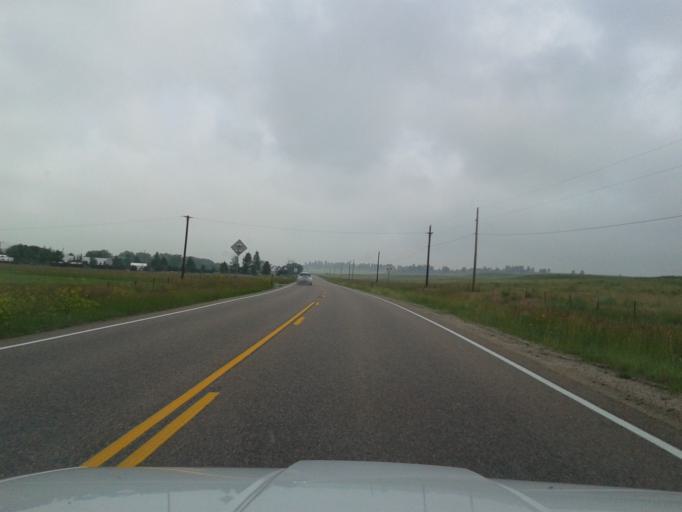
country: US
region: Colorado
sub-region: Elbert County
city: Elizabeth
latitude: 39.2378
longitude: -104.6962
